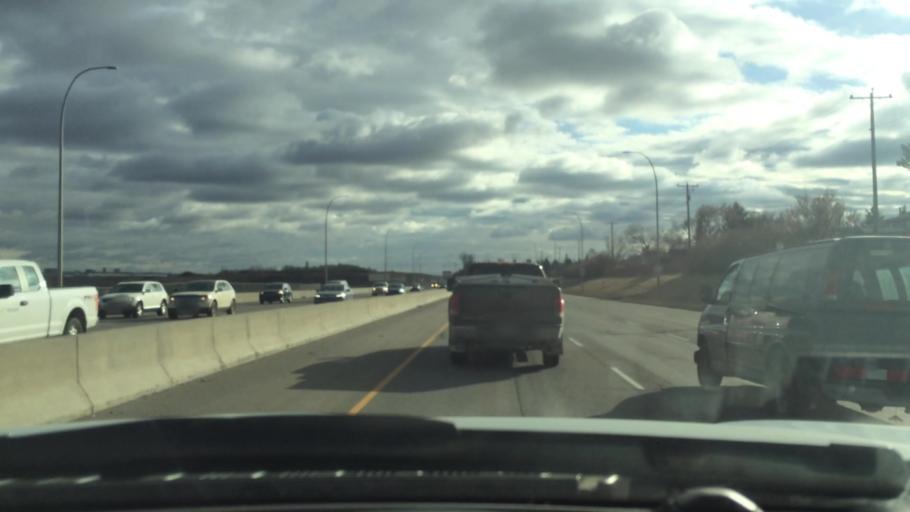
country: CA
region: Alberta
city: Calgary
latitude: 51.1326
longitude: -114.0667
